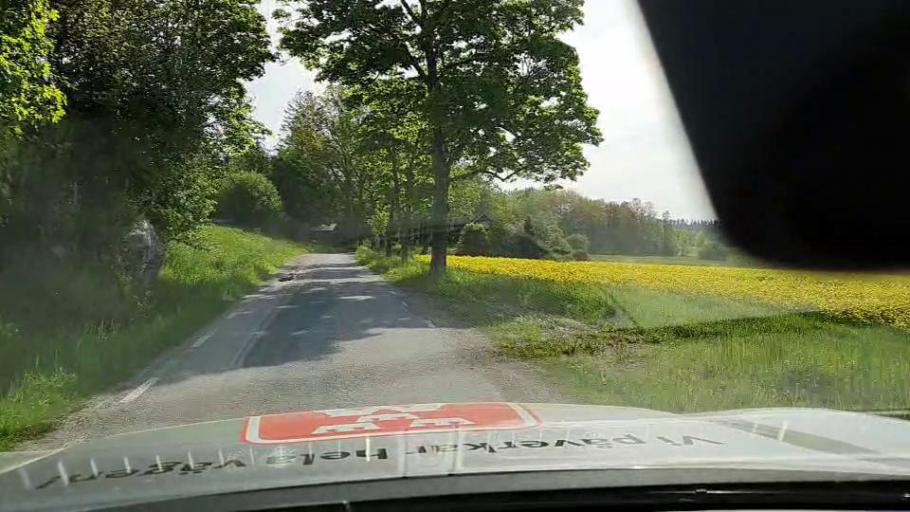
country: SE
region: Soedermanland
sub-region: Eskilstuna Kommun
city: Arla
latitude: 59.2568
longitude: 16.6878
